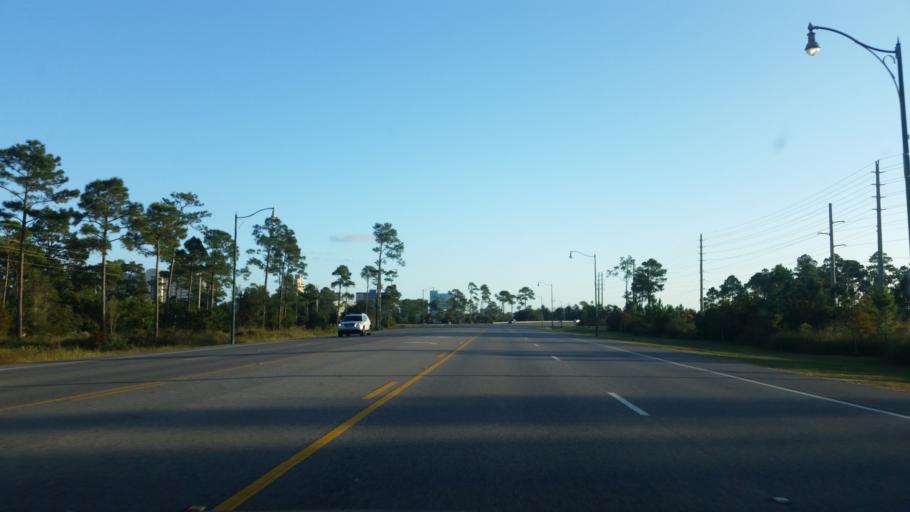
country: US
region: Alabama
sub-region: Baldwin County
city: Orange Beach
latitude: 30.2776
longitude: -87.5809
